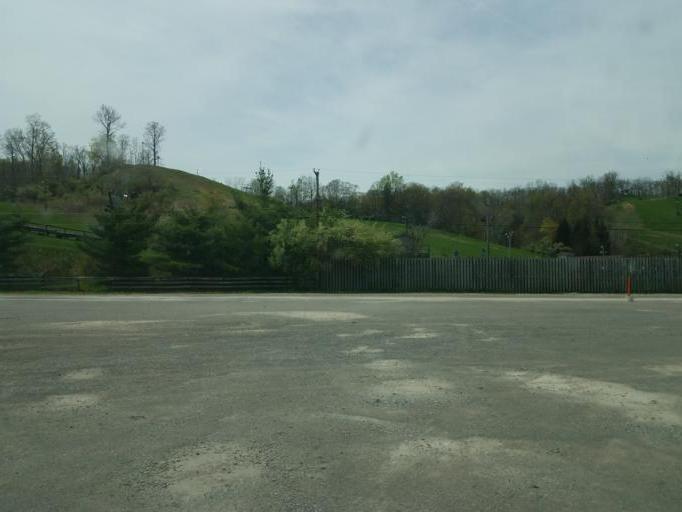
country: US
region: Ohio
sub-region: Summit County
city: Peninsula
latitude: 41.2642
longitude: -81.5626
